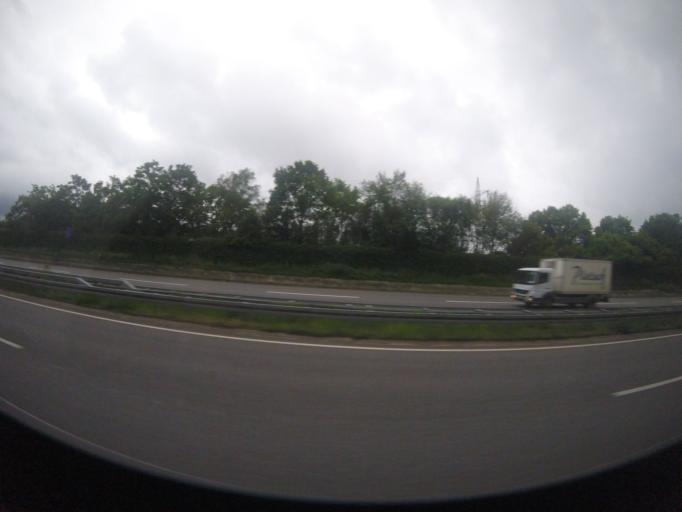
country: DE
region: Saarland
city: Spiesen-Elversberg
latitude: 49.3213
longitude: 7.1412
